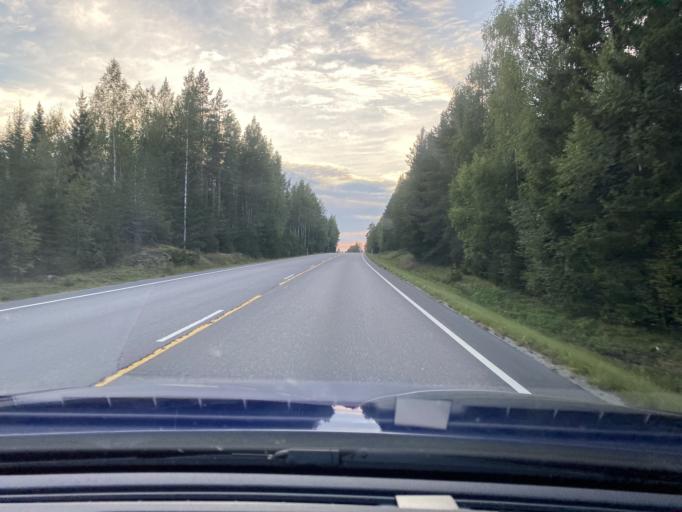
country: FI
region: Satakunta
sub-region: Pohjois-Satakunta
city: Kankaanpaeae
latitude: 61.7692
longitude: 22.4693
